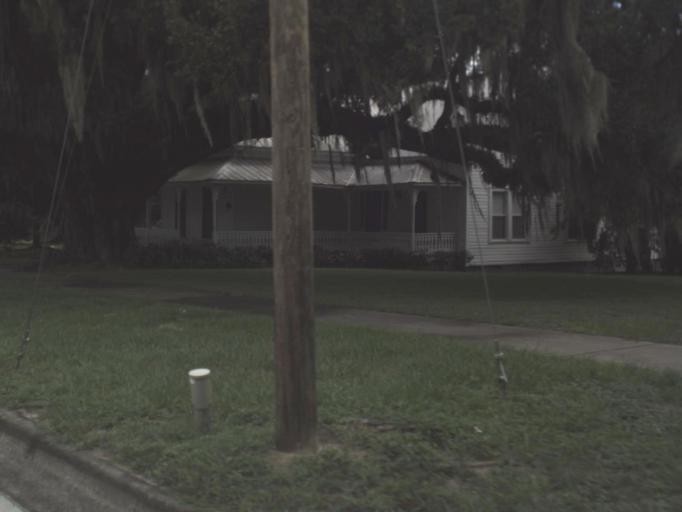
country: US
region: Florida
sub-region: Polk County
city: Fort Meade
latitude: 27.7520
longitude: -81.7940
